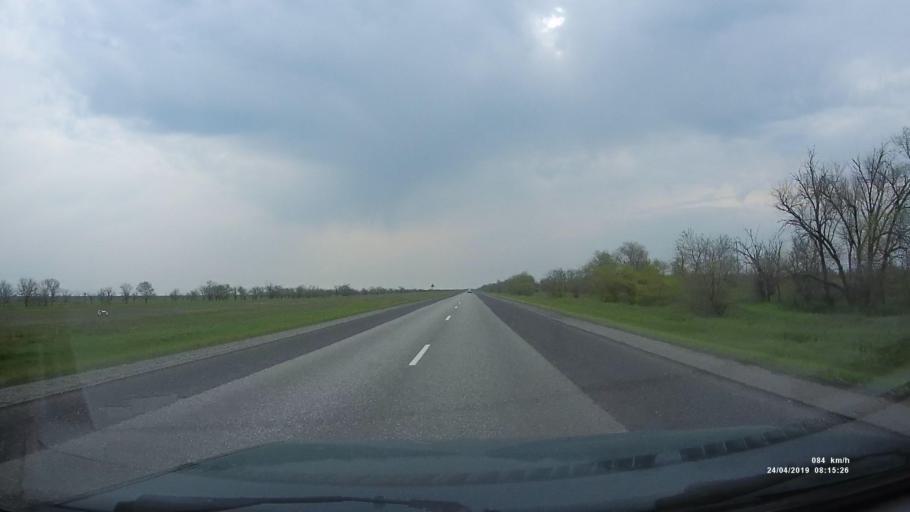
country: RU
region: Kalmykiya
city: Priyutnoye
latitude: 46.0997
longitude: 43.5937
